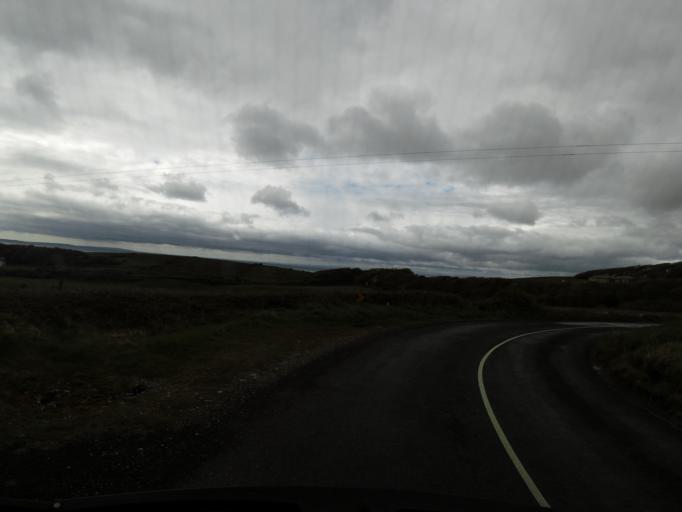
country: IE
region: Connaught
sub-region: County Galway
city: Bearna
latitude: 53.0434
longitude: -9.3386
